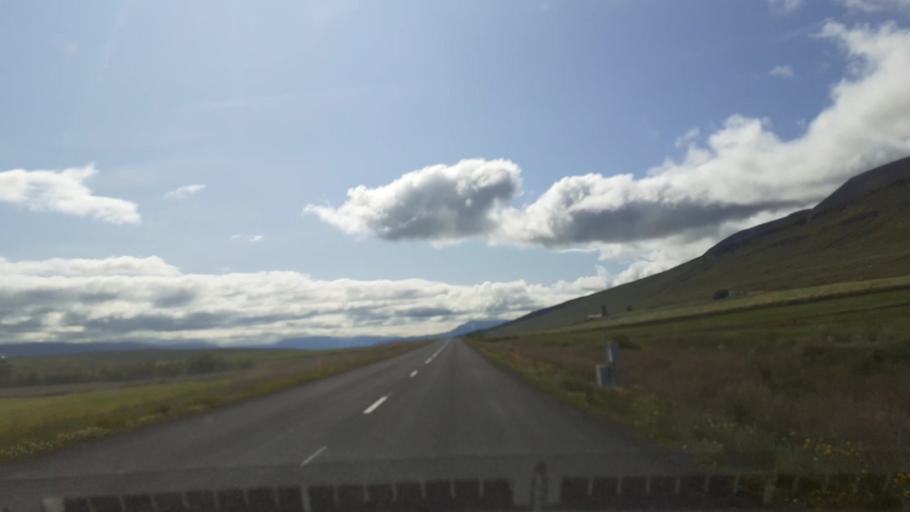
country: IS
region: Northeast
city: Akureyri
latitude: 65.8639
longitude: -18.2614
